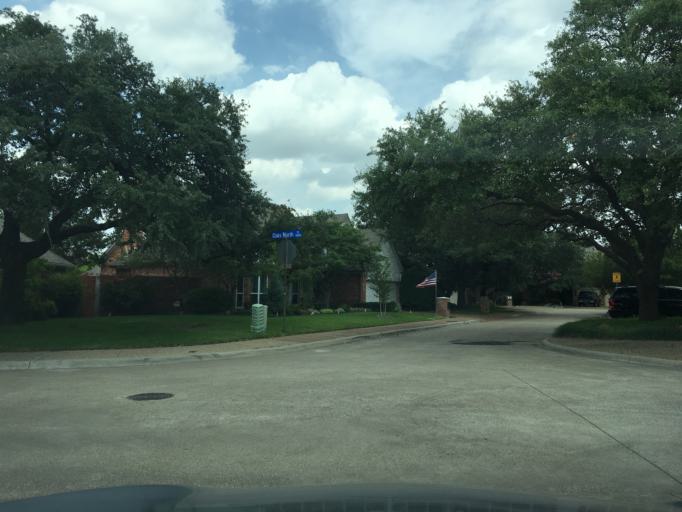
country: US
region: Texas
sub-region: Dallas County
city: Addison
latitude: 32.9500
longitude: -96.8155
